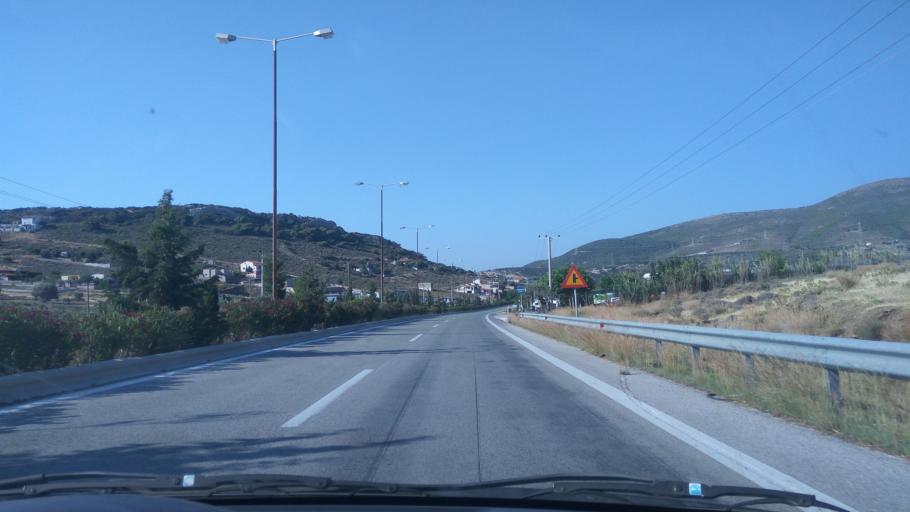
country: GR
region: Attica
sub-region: Nomarchia Anatolikis Attikis
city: Lavrio
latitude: 37.7814
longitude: 24.0573
